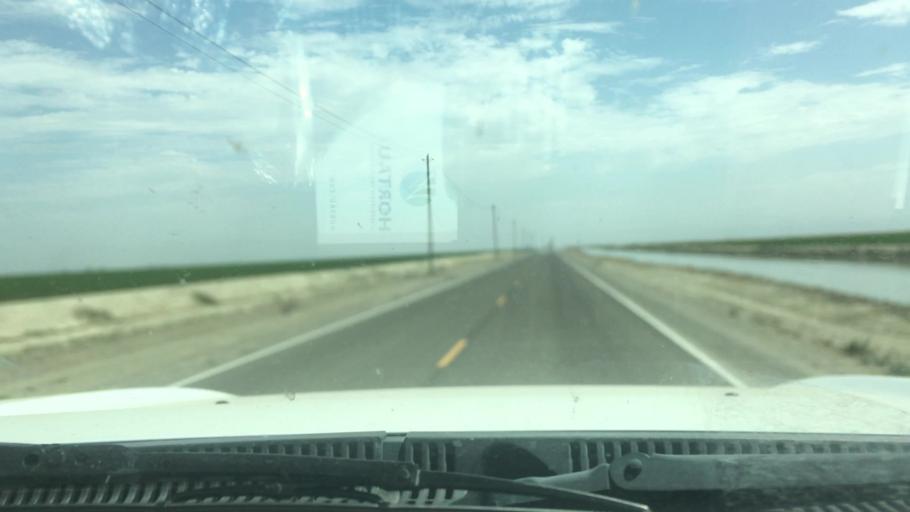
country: US
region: California
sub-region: Tulare County
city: Alpaugh
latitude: 35.8973
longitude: -119.5734
